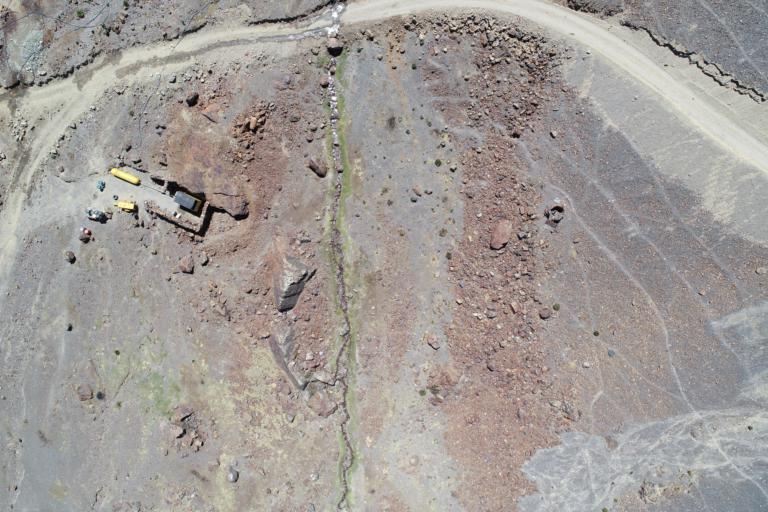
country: BO
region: La Paz
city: La Paz
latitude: -16.6208
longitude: -67.8255
